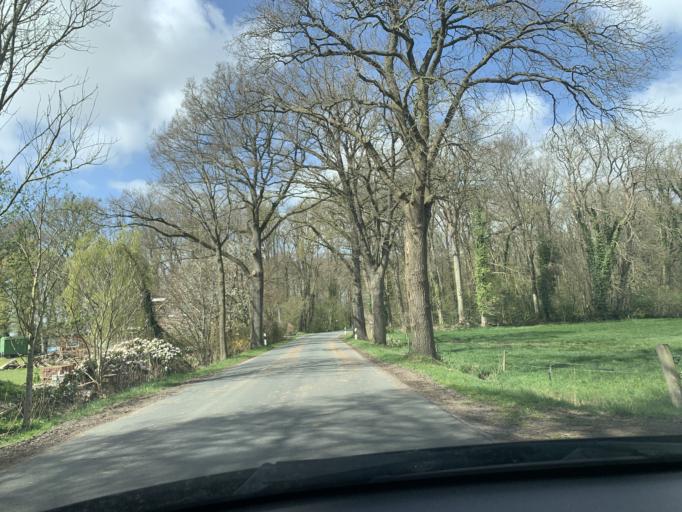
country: DE
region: Lower Saxony
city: Westerstede
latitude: 53.3100
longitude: 7.9312
